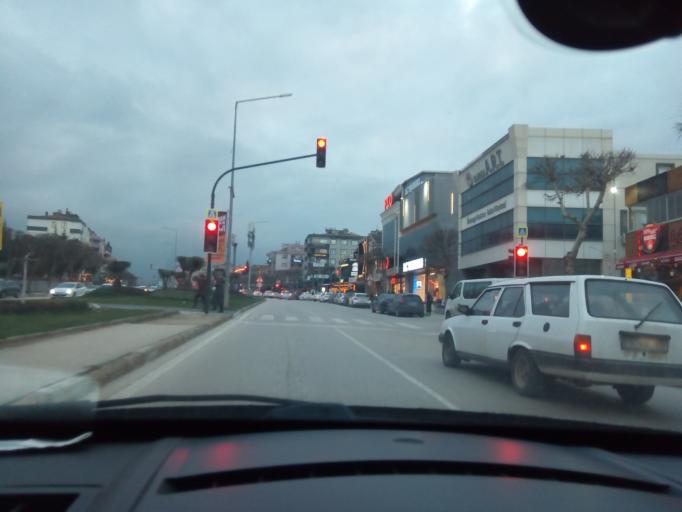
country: TR
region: Bursa
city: Yildirim
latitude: 40.2288
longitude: 28.9808
